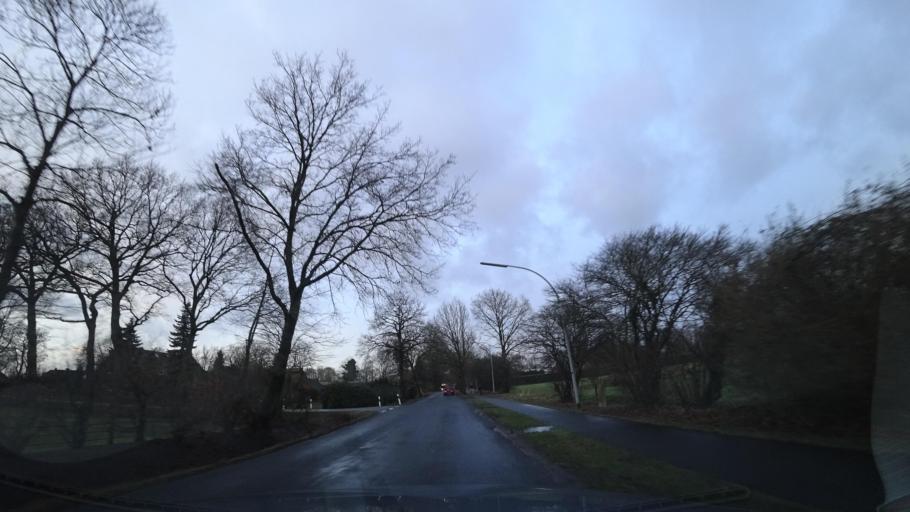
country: DE
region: Lower Saxony
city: Oldenburg
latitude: 53.1019
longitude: 8.2763
